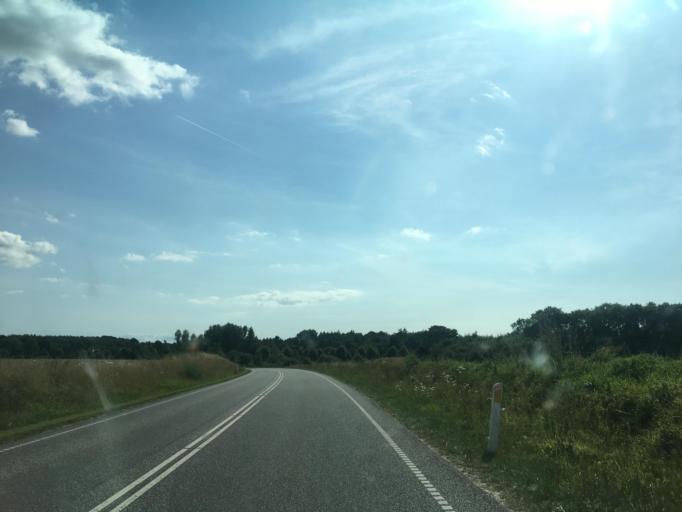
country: DK
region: South Denmark
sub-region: Middelfart Kommune
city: Ejby
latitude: 55.3965
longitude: 9.9639
